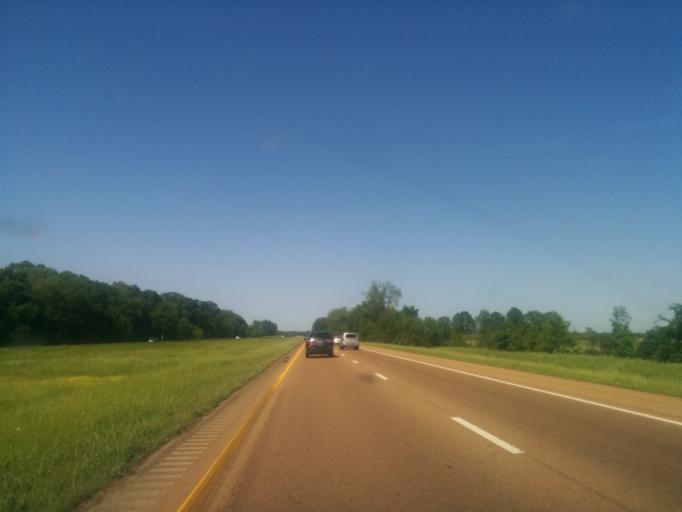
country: US
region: Mississippi
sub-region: Madison County
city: Madison
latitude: 32.4891
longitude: -90.1282
